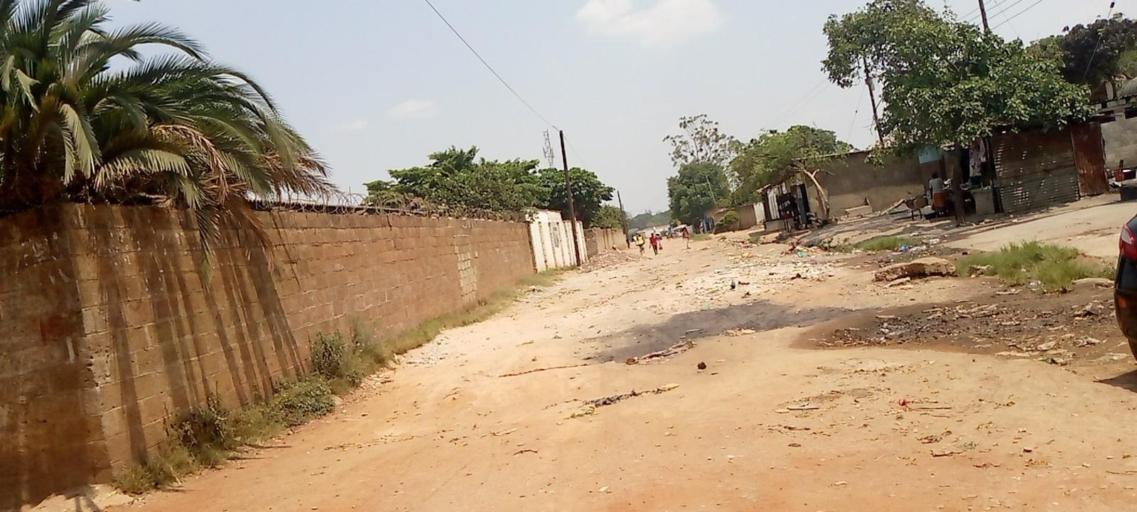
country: ZM
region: Lusaka
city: Lusaka
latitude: -15.4023
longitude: 28.3478
